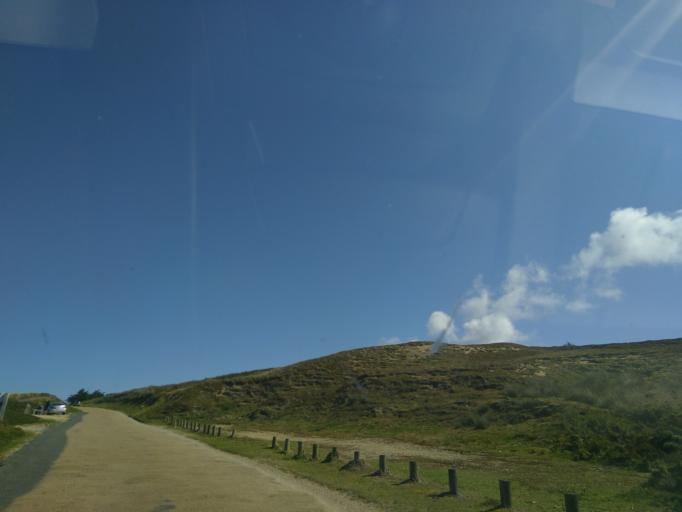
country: FR
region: Brittany
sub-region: Departement du Finistere
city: Camaret-sur-Mer
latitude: 48.2781
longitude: -4.6129
